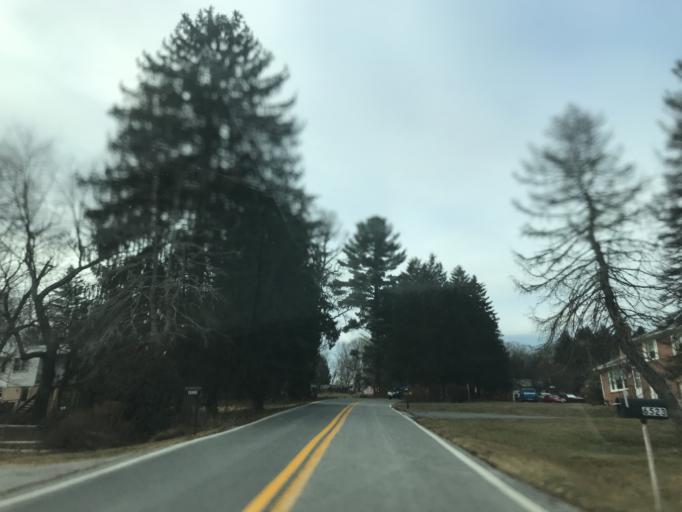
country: US
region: Maryland
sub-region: Carroll County
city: Eldersburg
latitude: 39.3930
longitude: -76.9190
